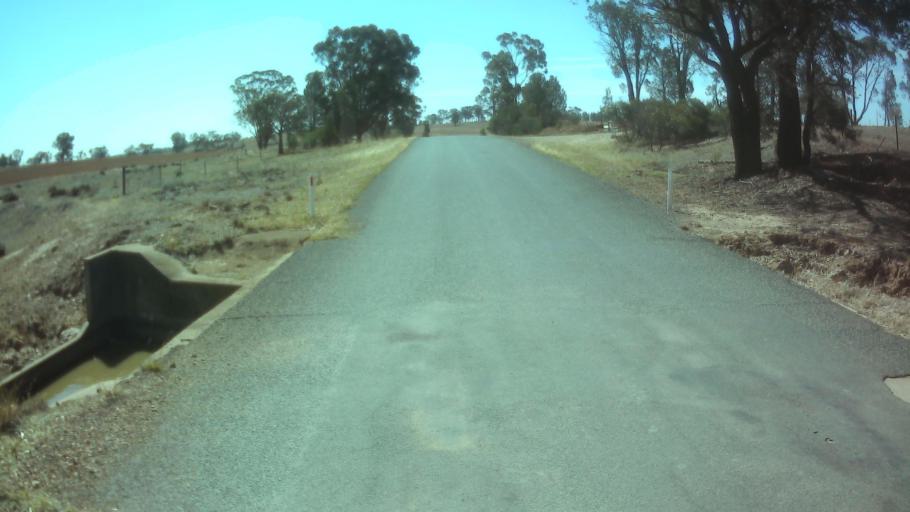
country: AU
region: New South Wales
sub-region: Weddin
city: Grenfell
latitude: -33.7626
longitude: 147.8624
